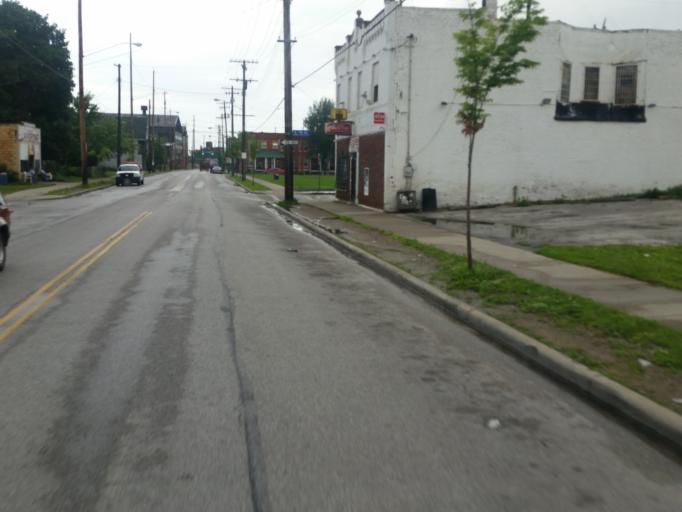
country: US
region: Ohio
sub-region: Cuyahoga County
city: Bratenahl
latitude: 41.4962
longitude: -81.6365
